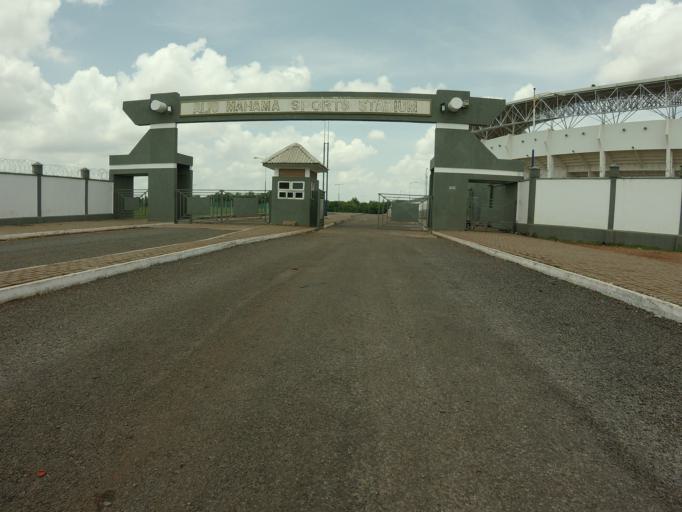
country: GH
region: Northern
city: Tamale
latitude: 9.4119
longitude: -0.8617
